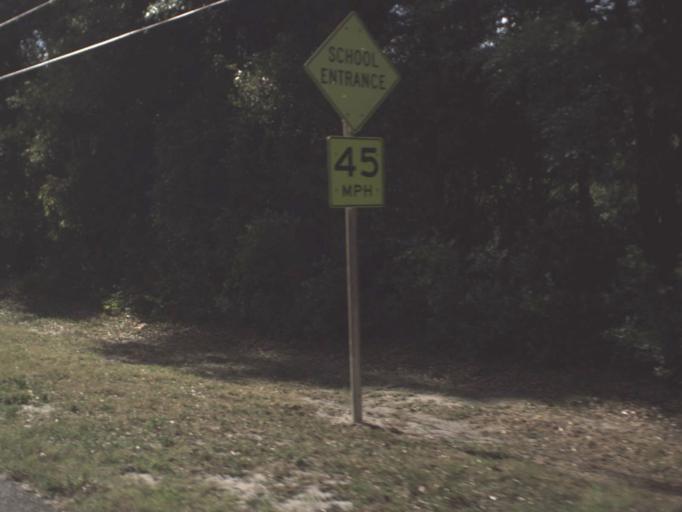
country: US
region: Florida
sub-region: Lake County
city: Mount Plymouth
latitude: 28.8128
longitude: -81.5152
